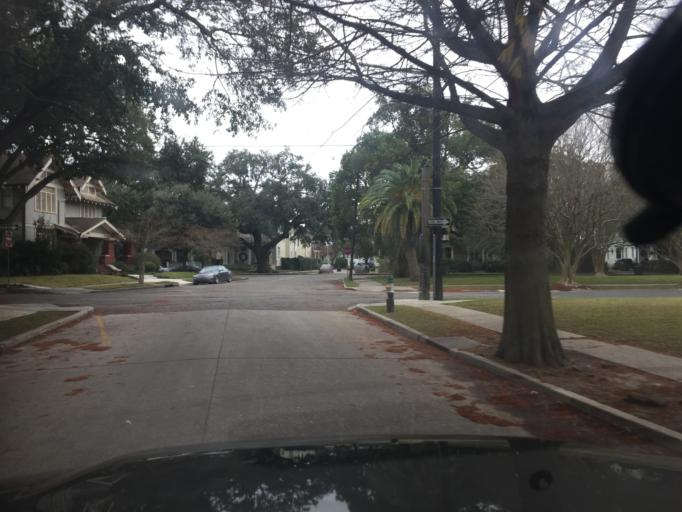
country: US
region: Louisiana
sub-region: Orleans Parish
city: New Orleans
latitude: 29.9776
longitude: -90.0842
